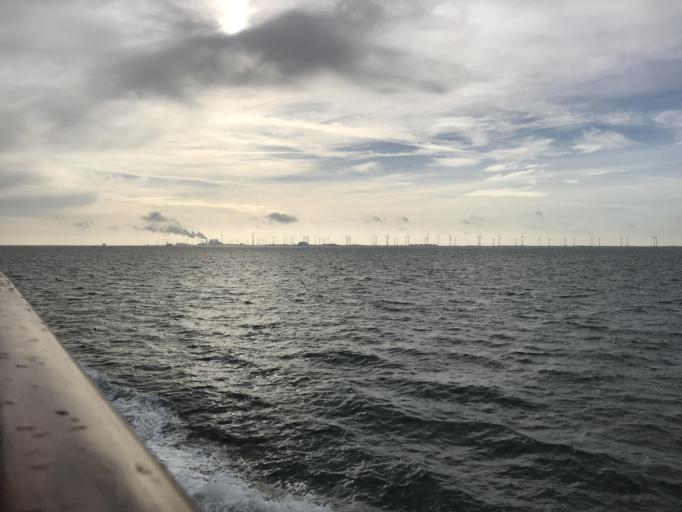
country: DE
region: Lower Saxony
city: Borkum
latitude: 53.5180
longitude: 6.7830
